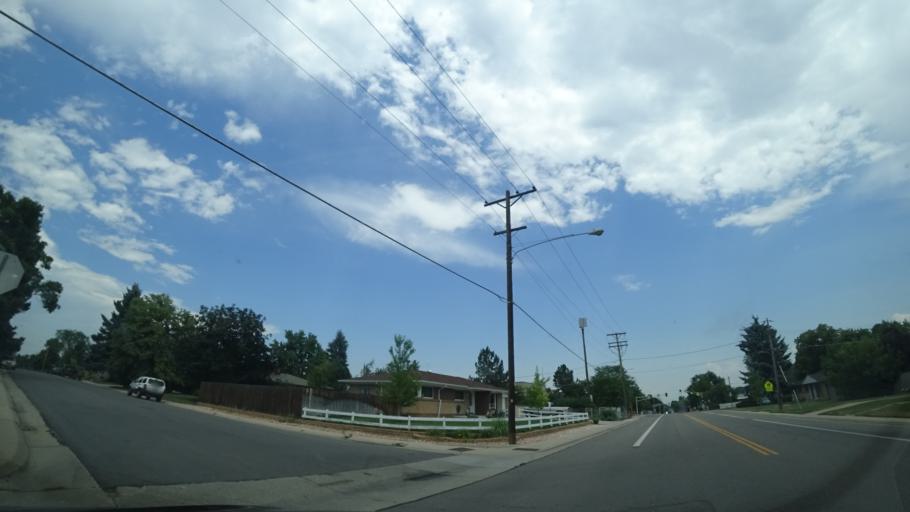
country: US
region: Colorado
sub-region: Jefferson County
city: Lakewood
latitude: 39.7185
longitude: -105.0941
